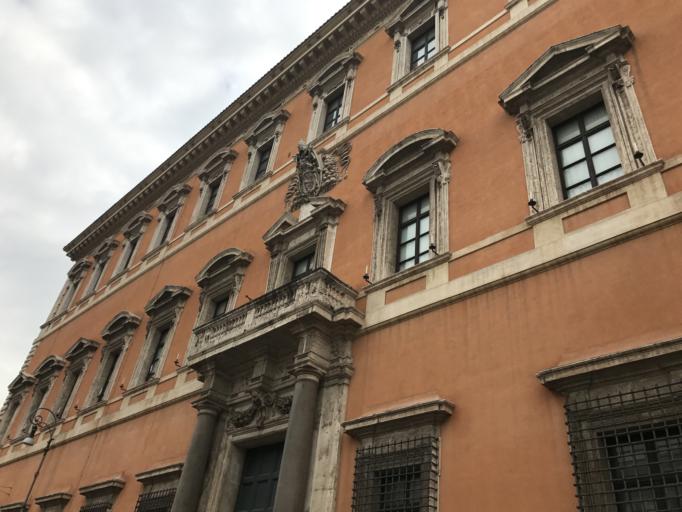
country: IT
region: Latium
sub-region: Citta metropolitana di Roma Capitale
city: Rome
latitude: 41.8871
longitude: 12.5054
